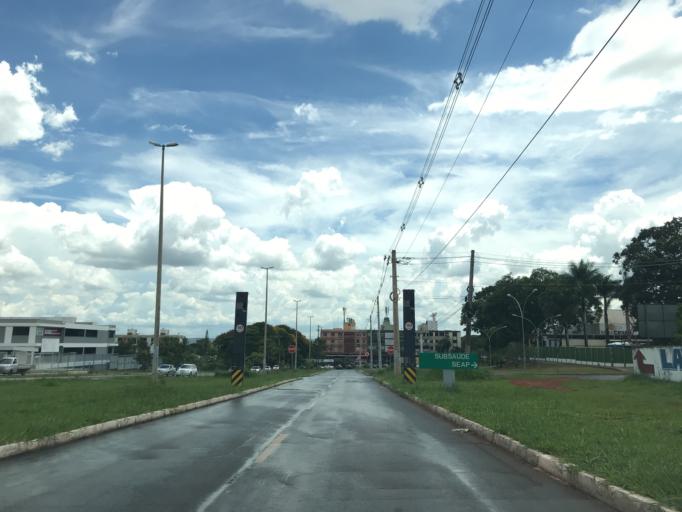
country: BR
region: Federal District
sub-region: Brasilia
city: Brasilia
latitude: -15.7646
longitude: -47.8960
